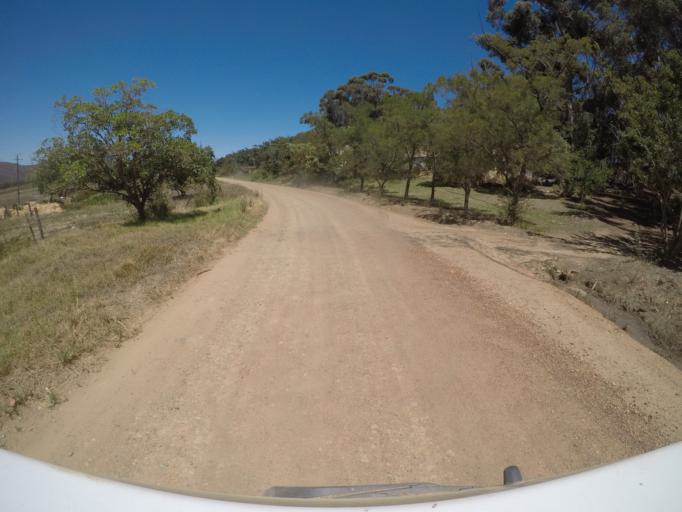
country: ZA
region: Western Cape
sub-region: Overberg District Municipality
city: Grabouw
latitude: -34.1646
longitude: 19.2239
